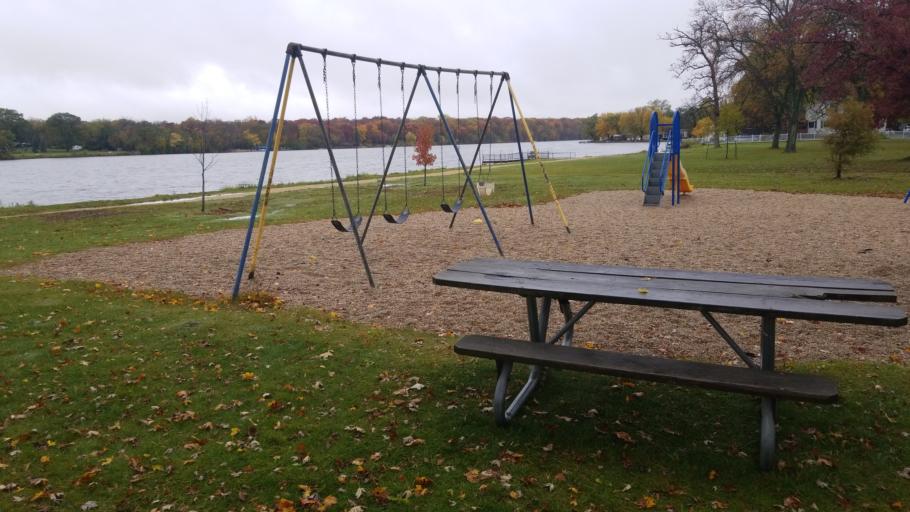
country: US
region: Wisconsin
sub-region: Rock County
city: Beloit
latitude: 42.5265
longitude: -89.0356
